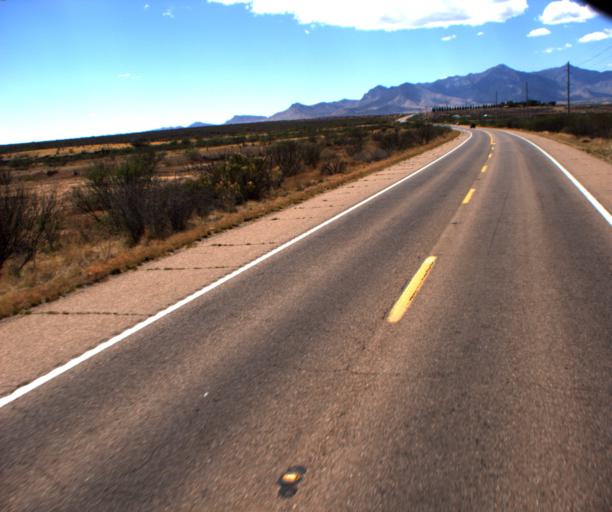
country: US
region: Arizona
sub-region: Cochise County
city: Naco
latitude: 31.3809
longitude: -110.0669
